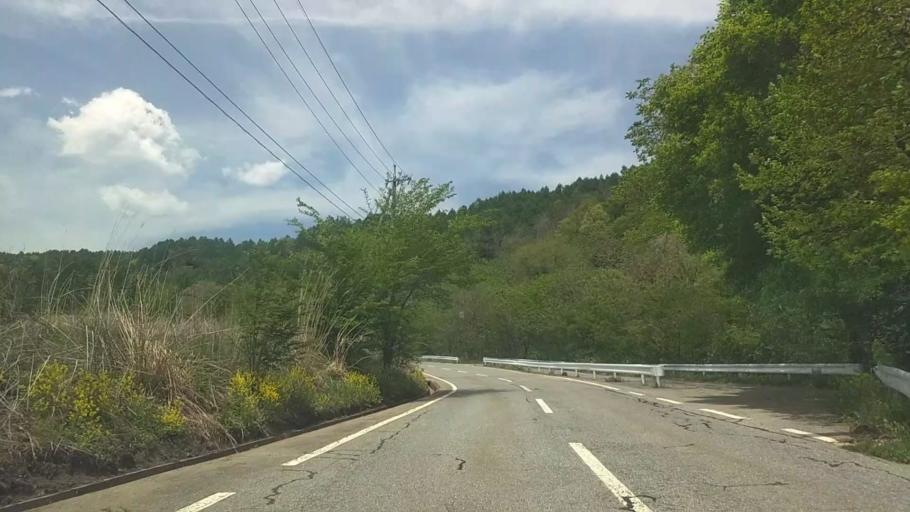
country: JP
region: Nagano
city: Saku
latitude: 36.1054
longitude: 138.4144
